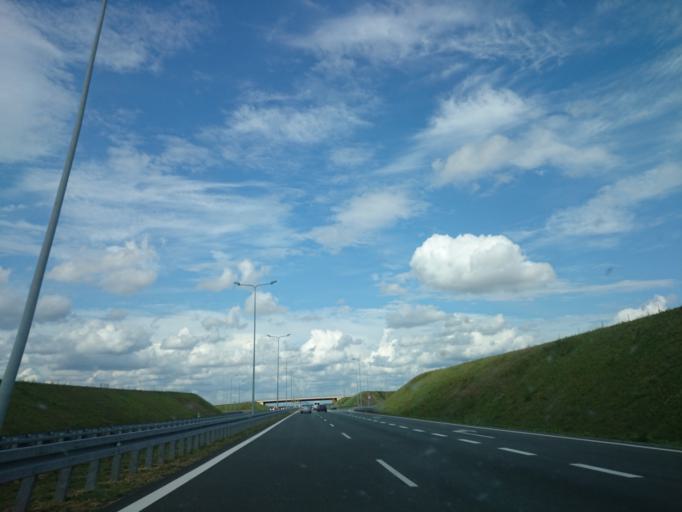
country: PL
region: Lubusz
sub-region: Powiat swiebodzinski
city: Swiebodzin
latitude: 52.2273
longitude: 15.5551
